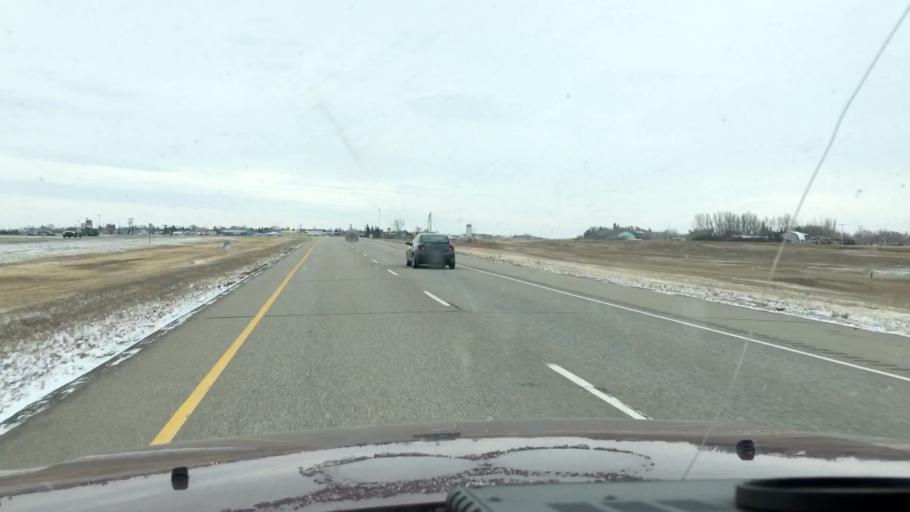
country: CA
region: Saskatchewan
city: Watrous
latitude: 51.2766
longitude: -106.0102
